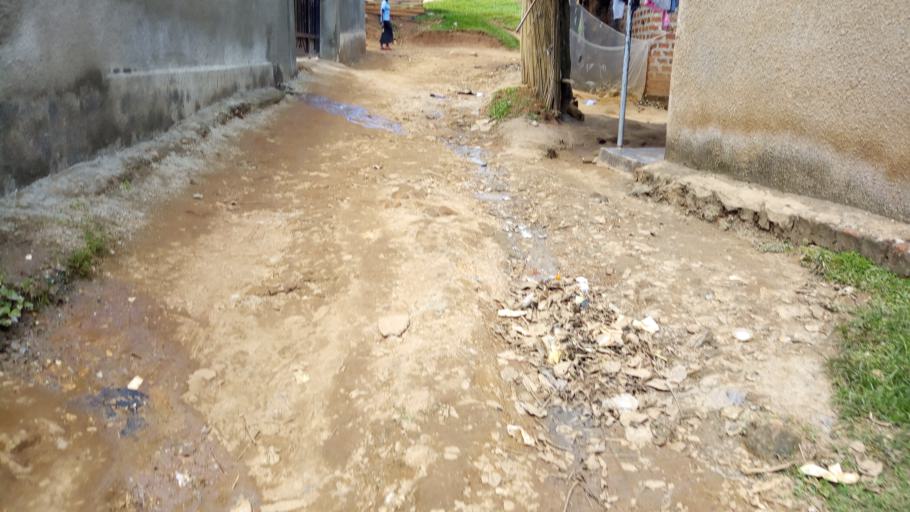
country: UG
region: Central Region
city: Kampala Central Division
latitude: 0.3566
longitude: 32.5576
